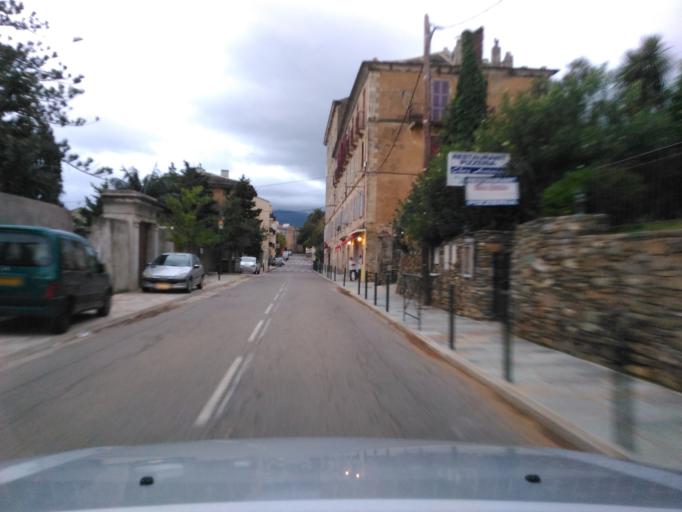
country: FR
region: Corsica
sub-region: Departement de la Haute-Corse
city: Brando
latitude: 42.7755
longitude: 9.4761
